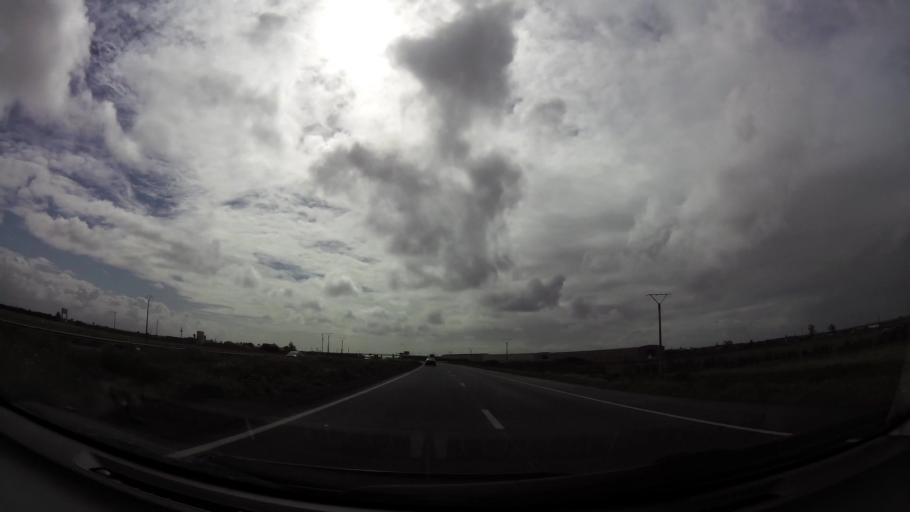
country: MA
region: Grand Casablanca
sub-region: Nouaceur
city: Dar Bouazza
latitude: 33.3531
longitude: -7.9870
